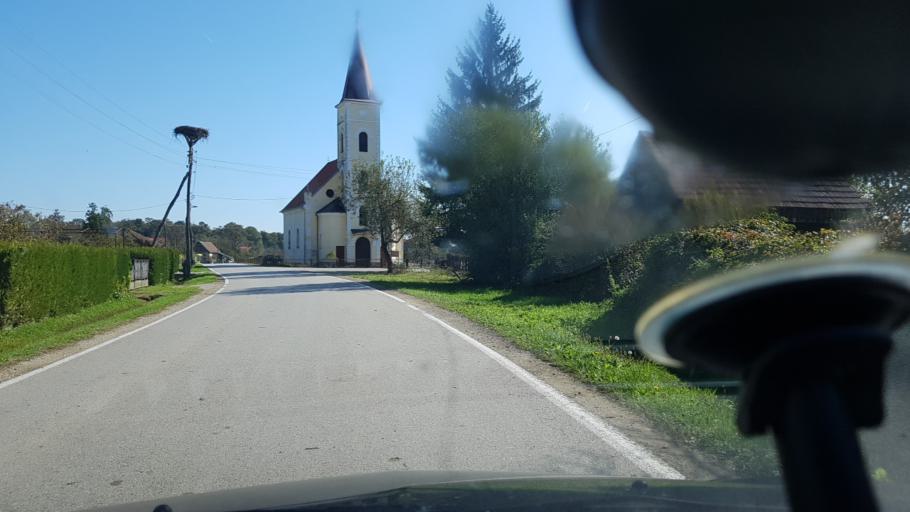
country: HR
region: Zagrebacka
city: Lupoglav
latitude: 45.7155
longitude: 16.3199
